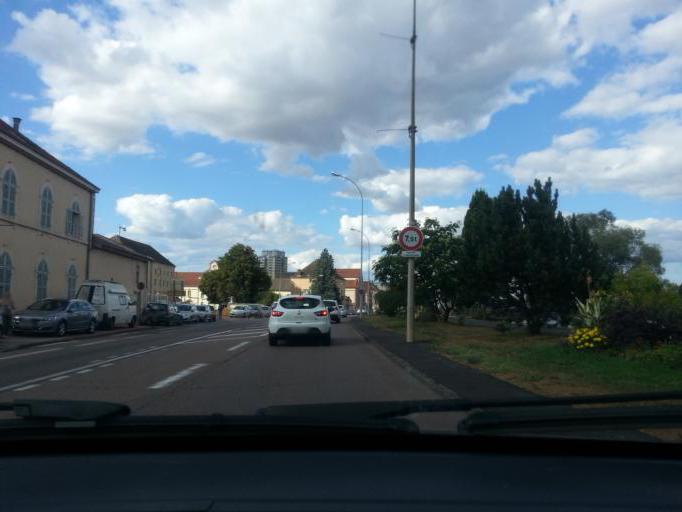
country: FR
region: Bourgogne
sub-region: Departement de Saone-et-Loire
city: Chalon-sur-Saone
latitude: 46.7748
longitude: 4.8456
